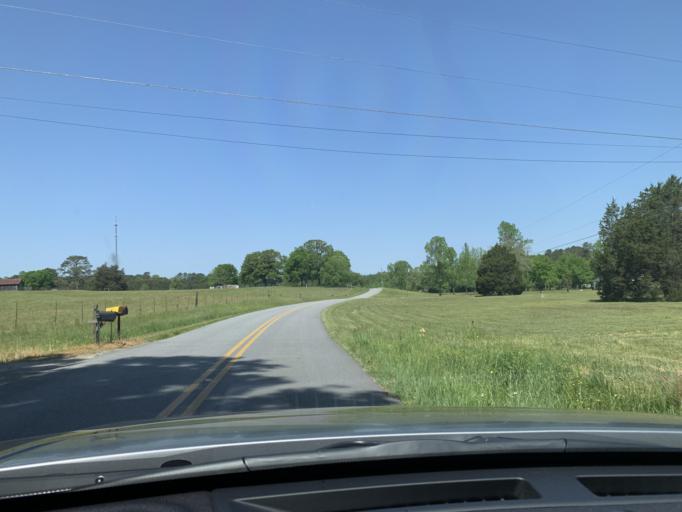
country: US
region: Georgia
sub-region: Polk County
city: Cedartown
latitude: 33.9838
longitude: -85.2205
